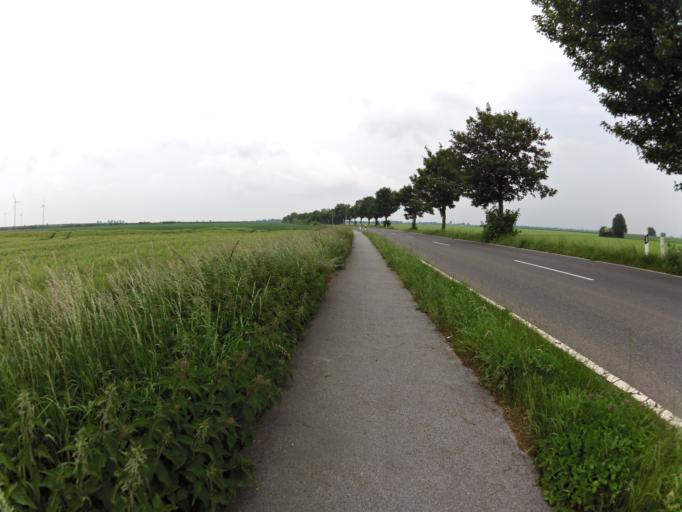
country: DE
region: North Rhine-Westphalia
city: Baesweiler
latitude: 50.9309
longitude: 6.1637
